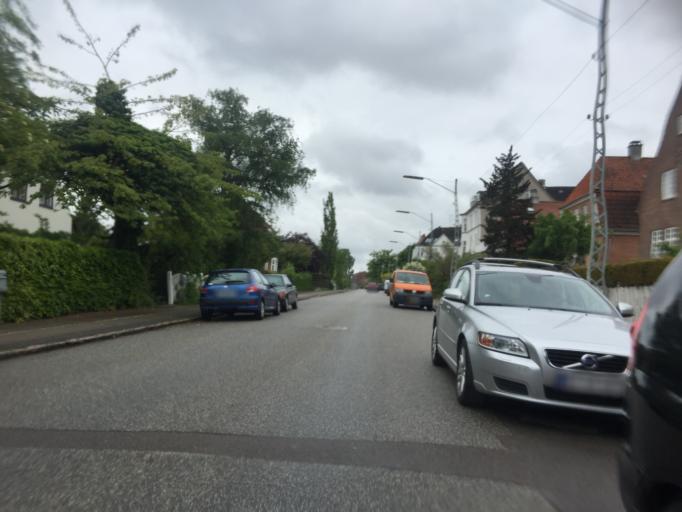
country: DK
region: Capital Region
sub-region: Frederiksberg Kommune
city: Frederiksberg
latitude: 55.6936
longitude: 12.5275
